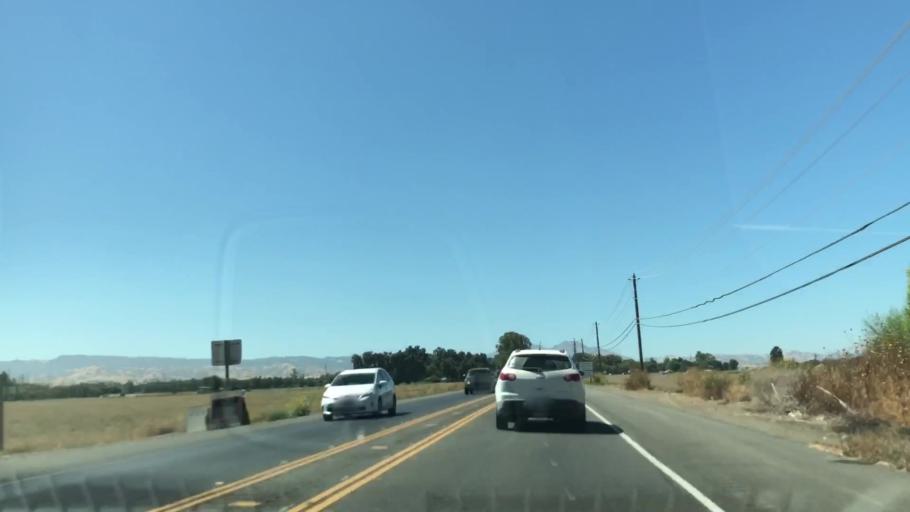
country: US
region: California
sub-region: Contra Costa County
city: Byron
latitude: 37.8893
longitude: -121.6323
